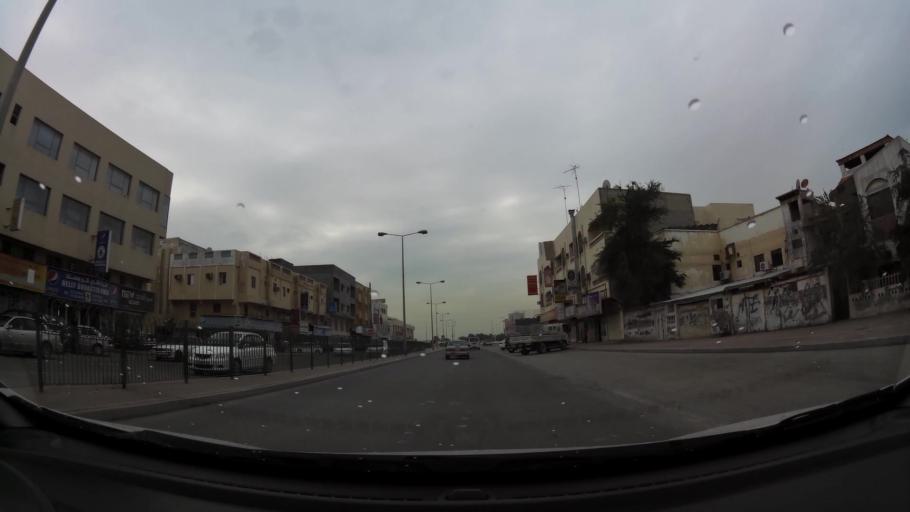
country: BH
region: Northern
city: Sitrah
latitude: 26.1651
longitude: 50.6077
